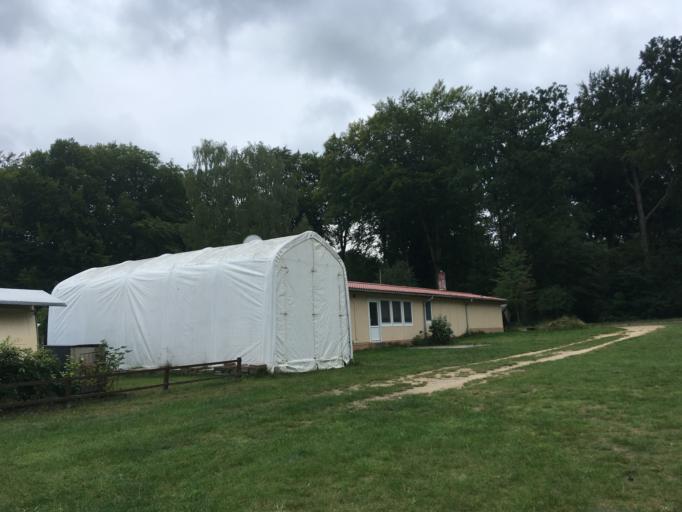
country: DE
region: Brandenburg
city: Gransee
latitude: 53.0744
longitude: 13.1751
